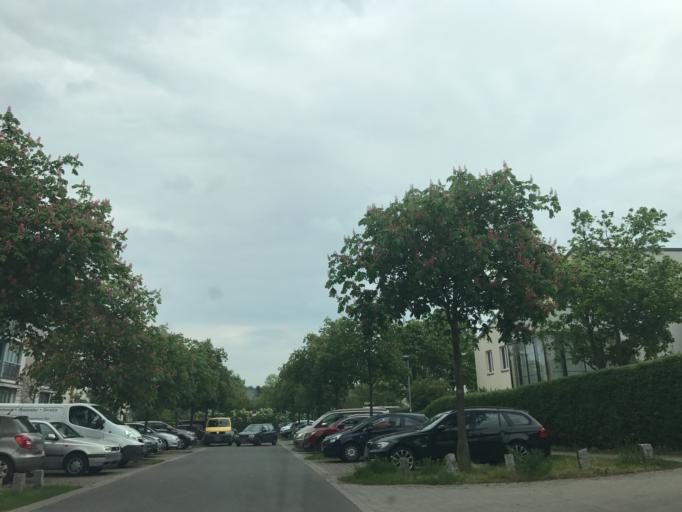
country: DE
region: Berlin
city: Staaken
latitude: 52.5602
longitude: 13.1387
